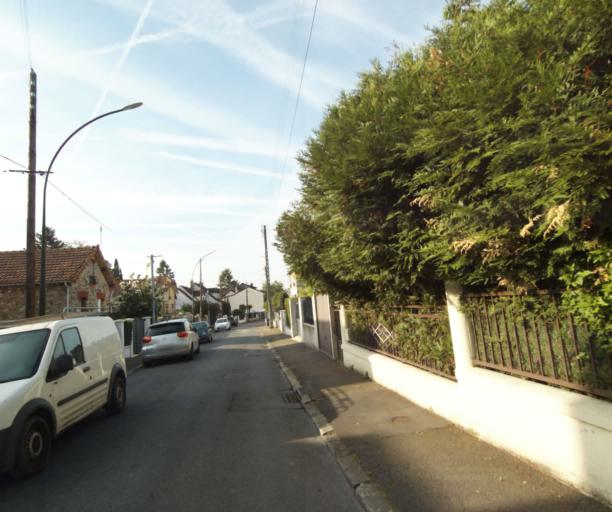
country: FR
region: Ile-de-France
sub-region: Departement du Val-d'Oise
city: Argenteuil
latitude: 48.9552
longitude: 2.2589
